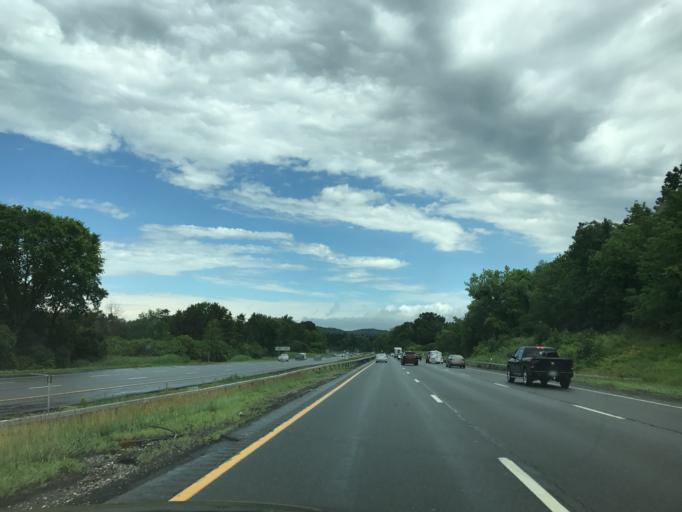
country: US
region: New York
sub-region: Albany County
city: Cohoes
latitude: 42.7818
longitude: -73.7588
